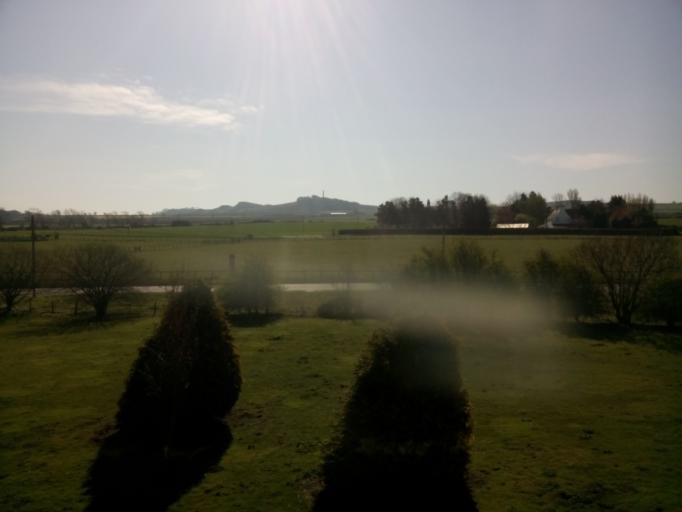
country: GB
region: Scotland
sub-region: East Lothian
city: Gullane
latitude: 55.9926
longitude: -2.8324
